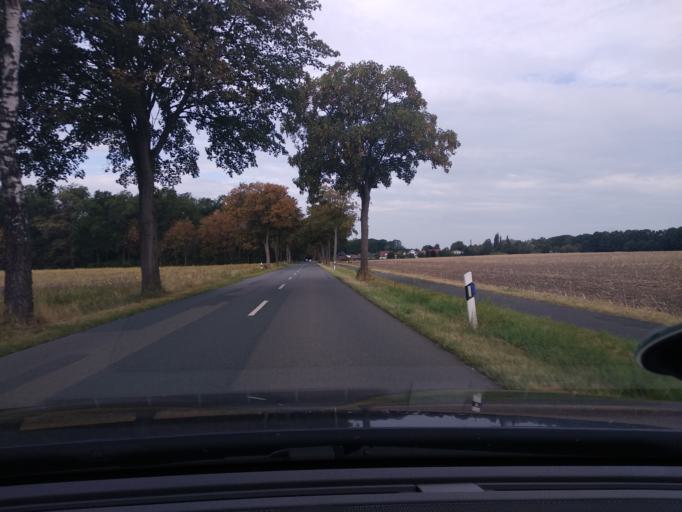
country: DE
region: Lower Saxony
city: Wagenhoff
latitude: 52.5096
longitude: 10.4941
